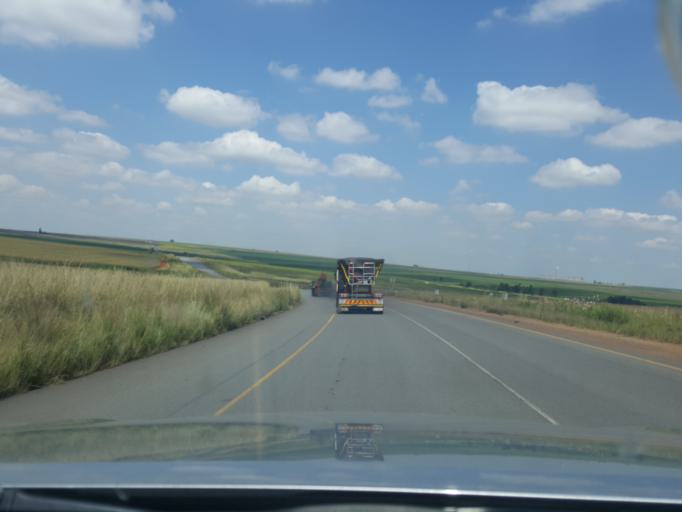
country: ZA
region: Mpumalanga
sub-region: Nkangala District Municipality
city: Witbank
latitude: -26.0209
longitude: 29.4257
